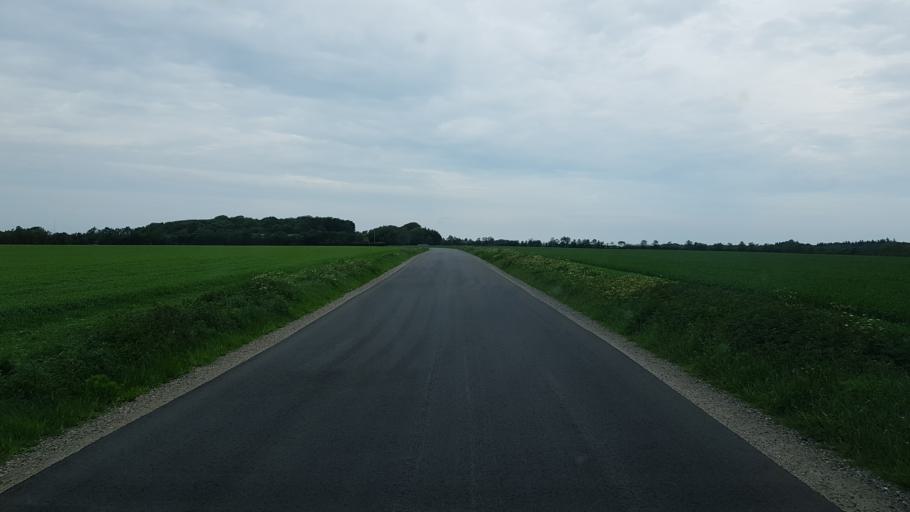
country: DK
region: South Denmark
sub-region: Varde Kommune
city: Oksbol
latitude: 55.7394
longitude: 8.3737
